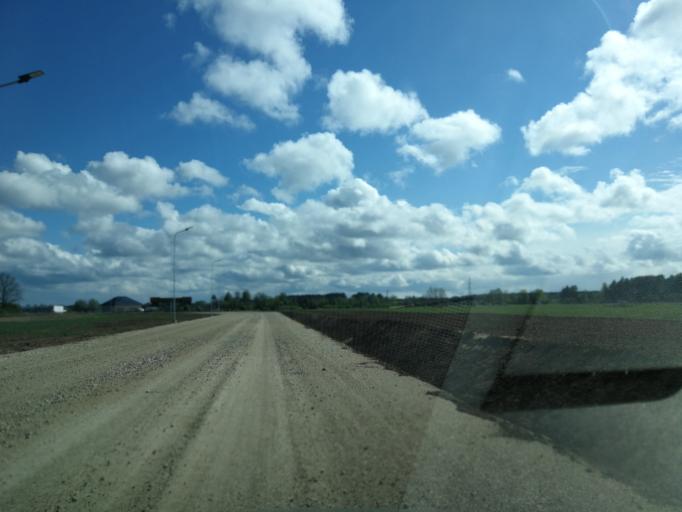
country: LV
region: Adazi
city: Adazi
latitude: 57.0949
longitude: 24.3039
